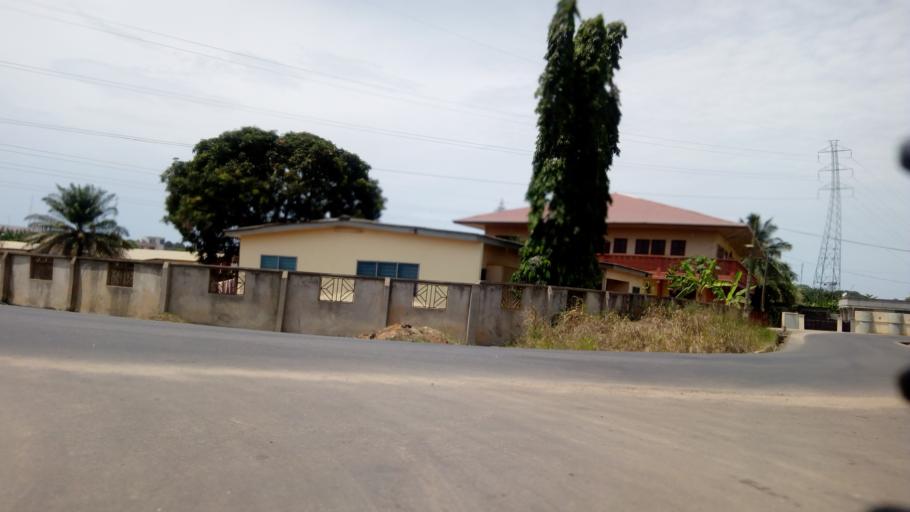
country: GH
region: Central
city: Cape Coast
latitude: 5.1231
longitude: -1.2758
